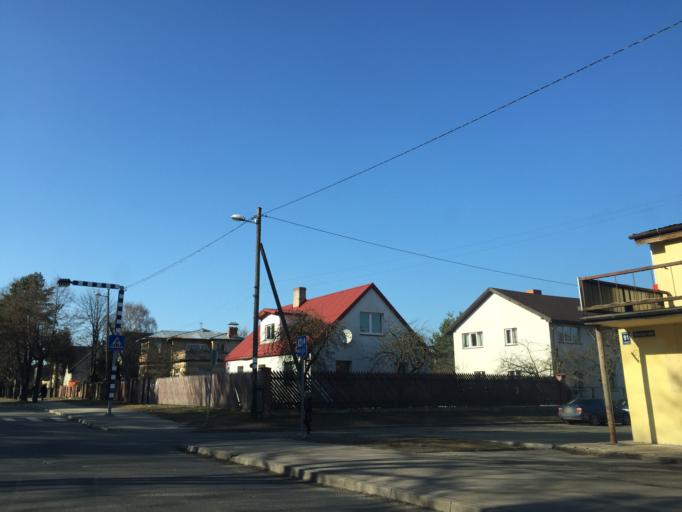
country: LV
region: Riga
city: Bergi
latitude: 56.9788
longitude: 24.2501
